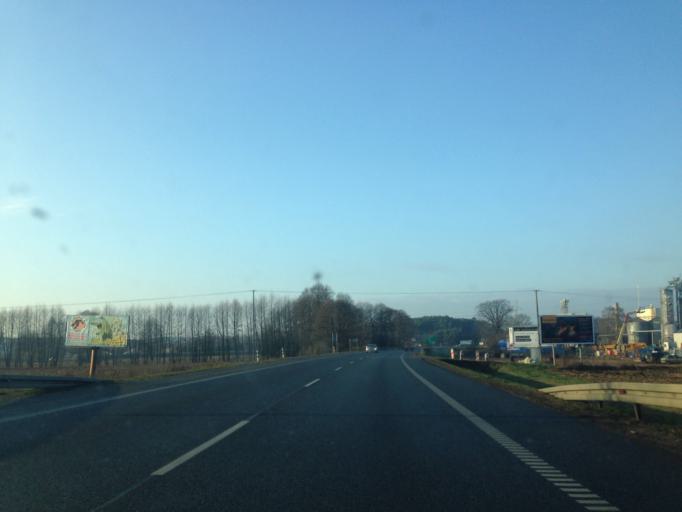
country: PL
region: Kujawsko-Pomorskie
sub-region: Powiat bydgoski
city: Solec Kujawski
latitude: 53.0649
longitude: 18.1680
